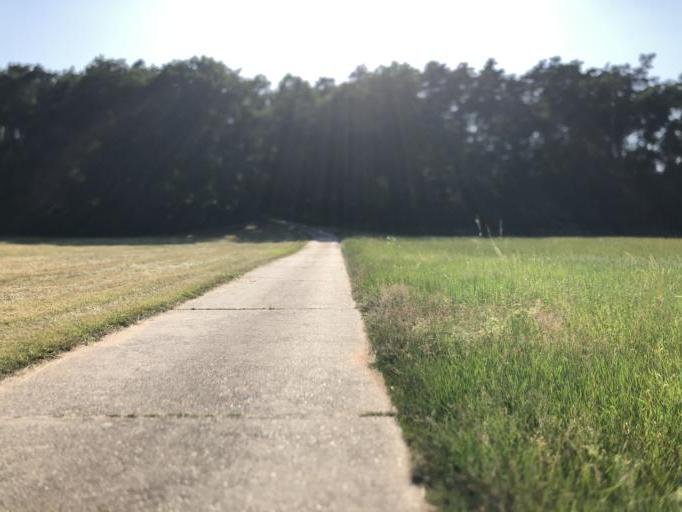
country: DE
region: Bavaria
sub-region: Regierungsbezirk Mittelfranken
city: Erlangen
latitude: 49.5572
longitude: 10.9763
